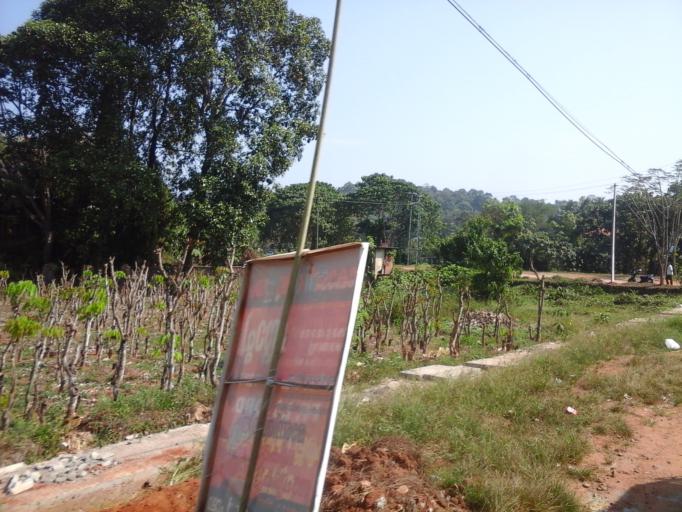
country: IN
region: Kerala
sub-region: Kottayam
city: Lalam
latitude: 9.7115
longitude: 76.6990
